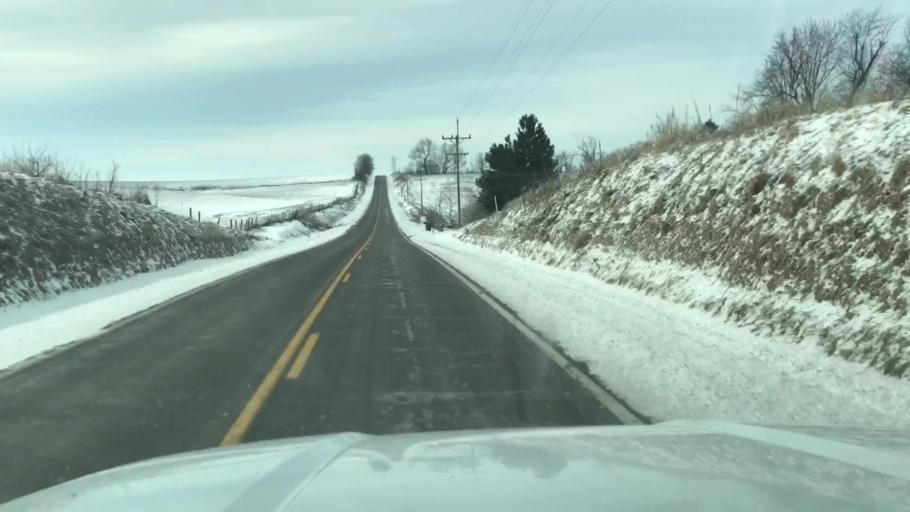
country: US
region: Missouri
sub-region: Holt County
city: Oregon
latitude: 40.0761
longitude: -95.1355
